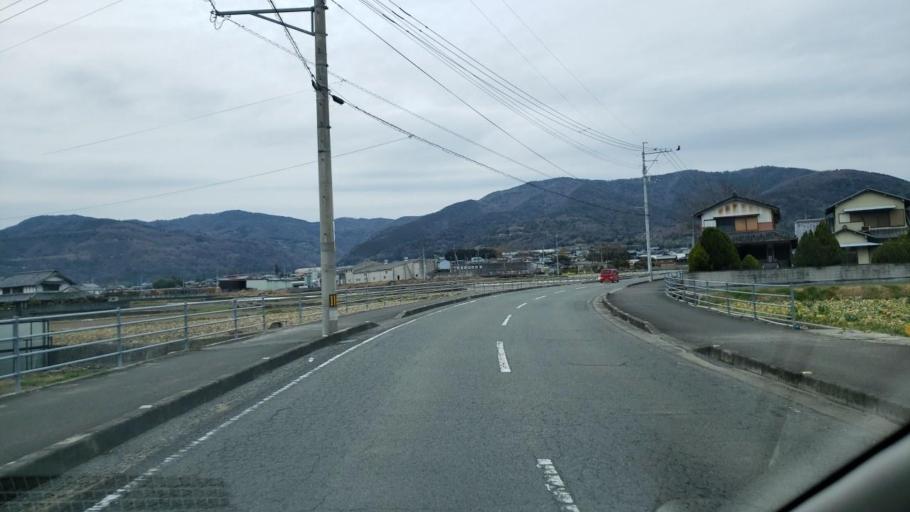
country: JP
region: Tokushima
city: Kamojimacho-jogejima
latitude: 34.1088
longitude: 134.3400
